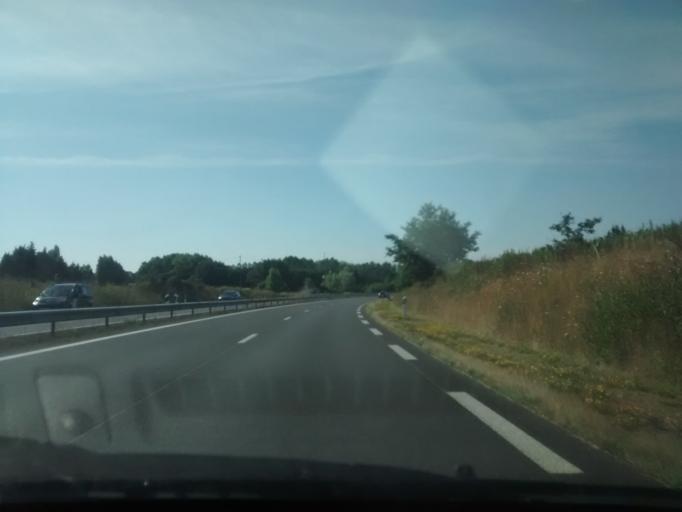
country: FR
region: Brittany
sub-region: Departement des Cotes-d'Armor
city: Pedernec
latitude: 48.5867
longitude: -3.2516
